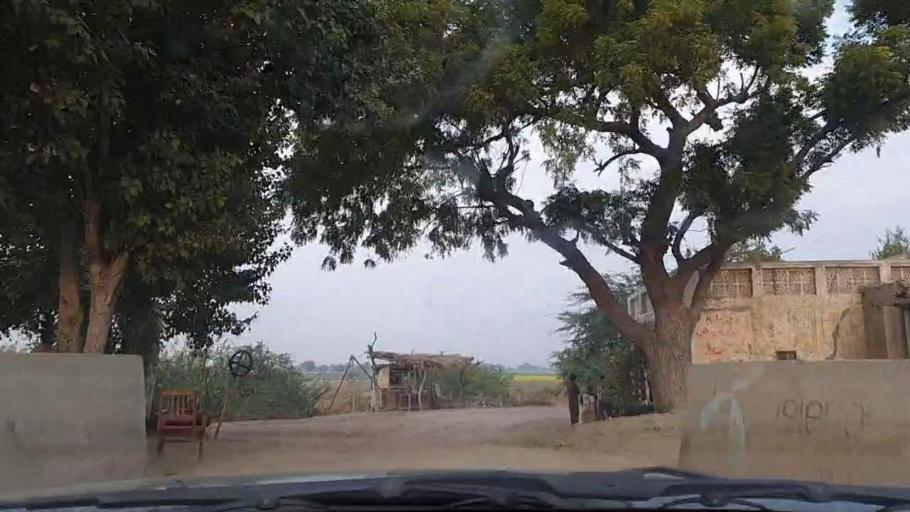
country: PK
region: Sindh
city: Pithoro
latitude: 25.5982
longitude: 69.4615
